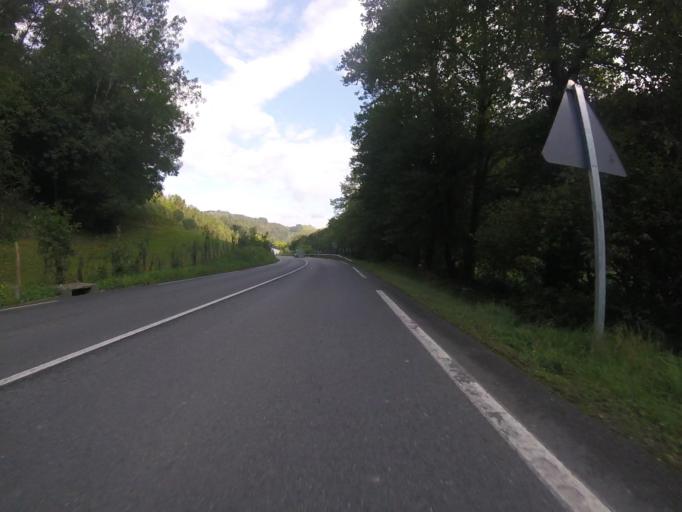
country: ES
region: Basque Country
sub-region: Provincia de Guipuzcoa
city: Amezqueta
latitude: 43.0705
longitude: -2.0845
